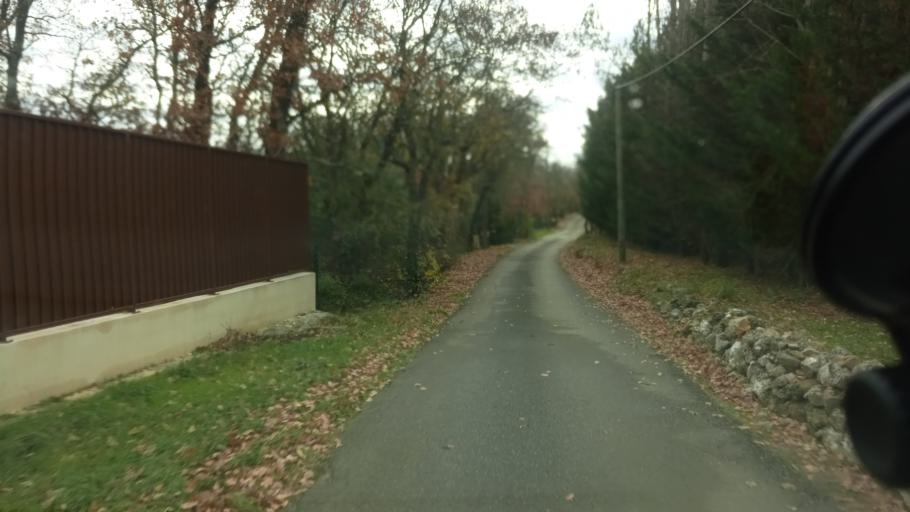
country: FR
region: Provence-Alpes-Cote d'Azur
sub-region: Departement du Var
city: Saint-Julien
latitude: 43.6311
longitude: 5.9294
